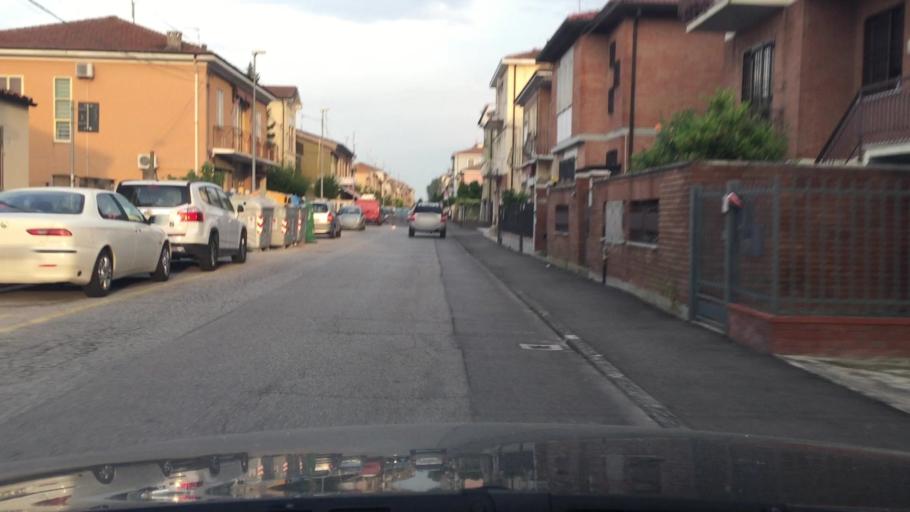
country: IT
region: Emilia-Romagna
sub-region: Provincia di Ferrara
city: Ferrara
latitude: 44.8227
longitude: 11.6092
